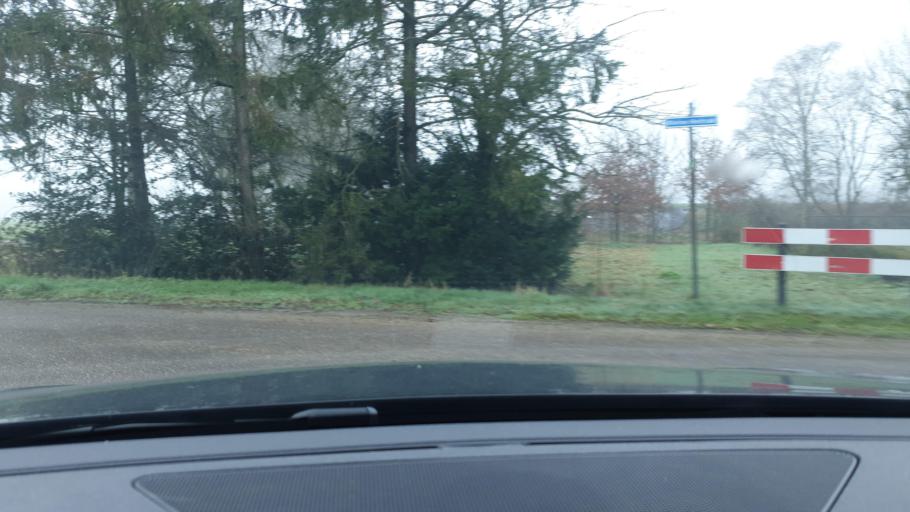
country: NL
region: North Brabant
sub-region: Gemeente Asten
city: Asten
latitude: 51.3695
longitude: 5.8485
